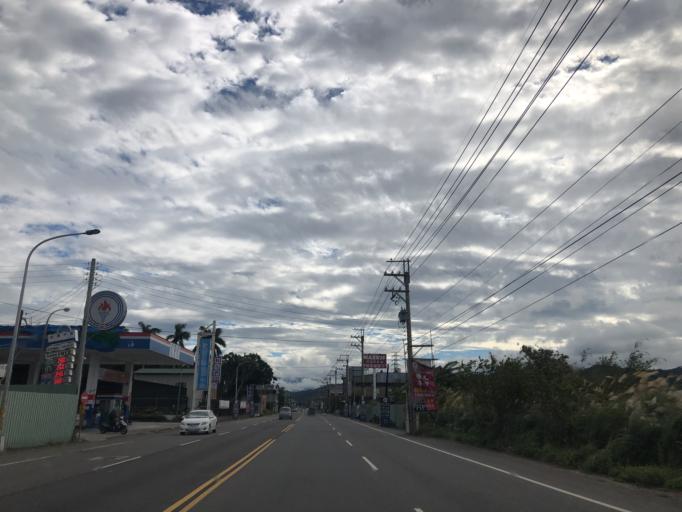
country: TW
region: Taiwan
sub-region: Hsinchu
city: Zhubei
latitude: 24.8217
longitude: 121.0948
